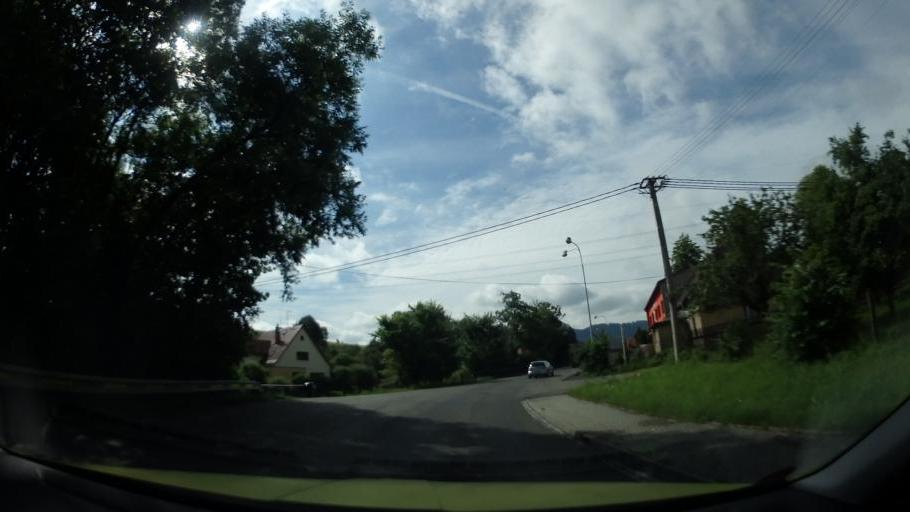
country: CZ
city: Hodslavice
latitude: 49.5445
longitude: 18.0252
